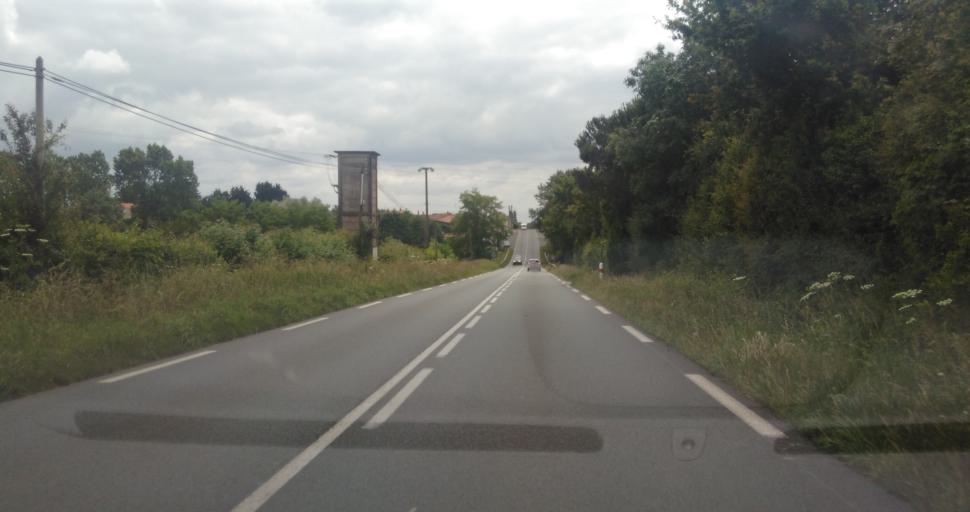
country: FR
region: Pays de la Loire
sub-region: Departement de la Vendee
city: Bournezeau
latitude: 46.6187
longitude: -1.1526
